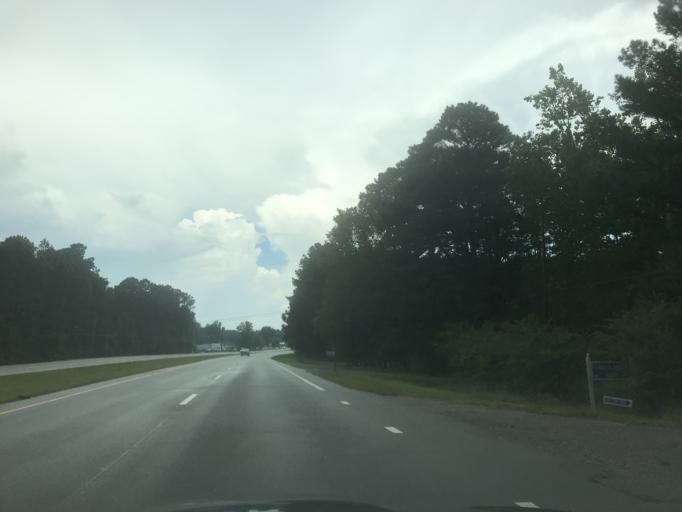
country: US
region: North Carolina
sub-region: Johnston County
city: Wilsons Mills
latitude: 35.5756
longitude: -78.3980
